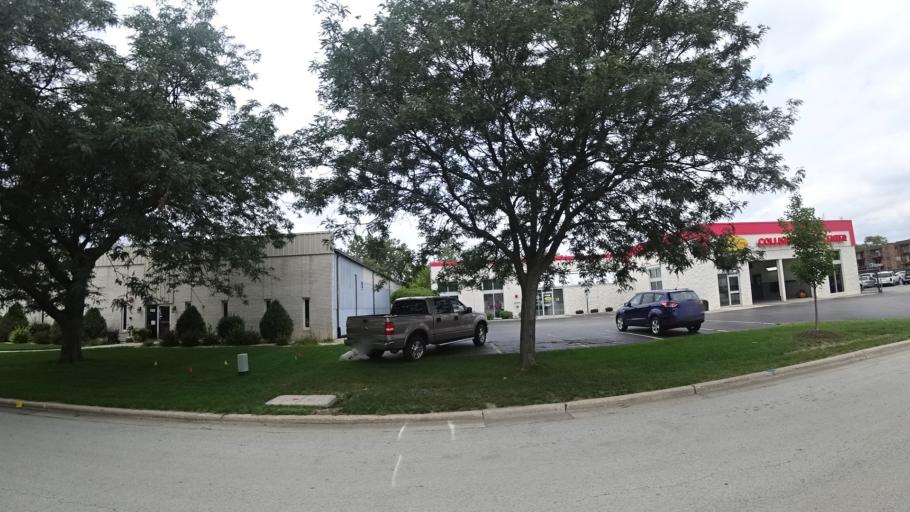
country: US
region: Illinois
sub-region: Cook County
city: Tinley Park
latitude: 41.5711
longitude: -87.7965
